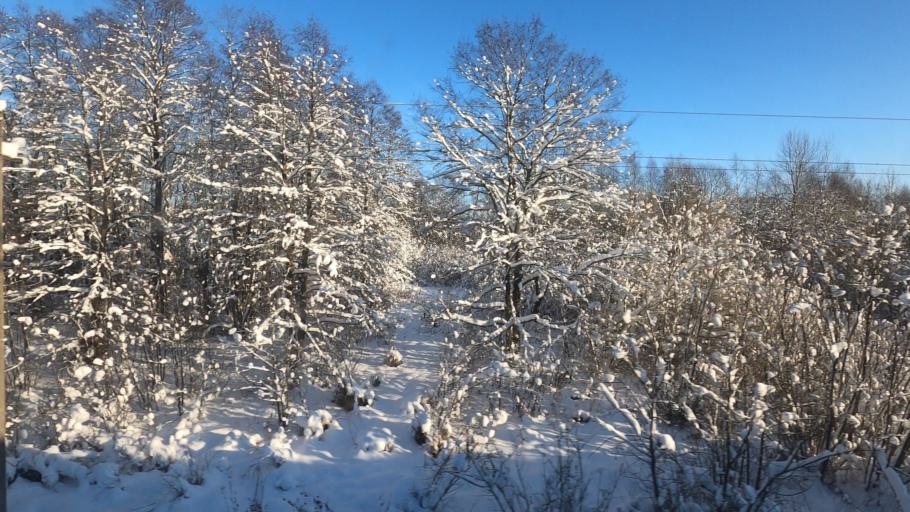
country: RU
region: Moskovskaya
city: Novo-Nikol'skoye
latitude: 56.6107
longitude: 37.5675
